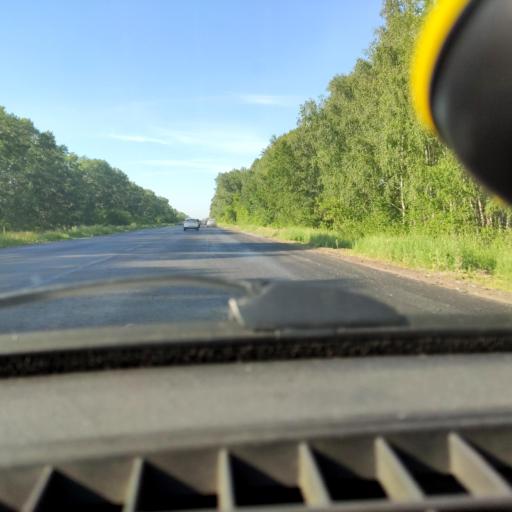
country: RU
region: Samara
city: Tol'yatti
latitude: 53.6455
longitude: 49.4215
